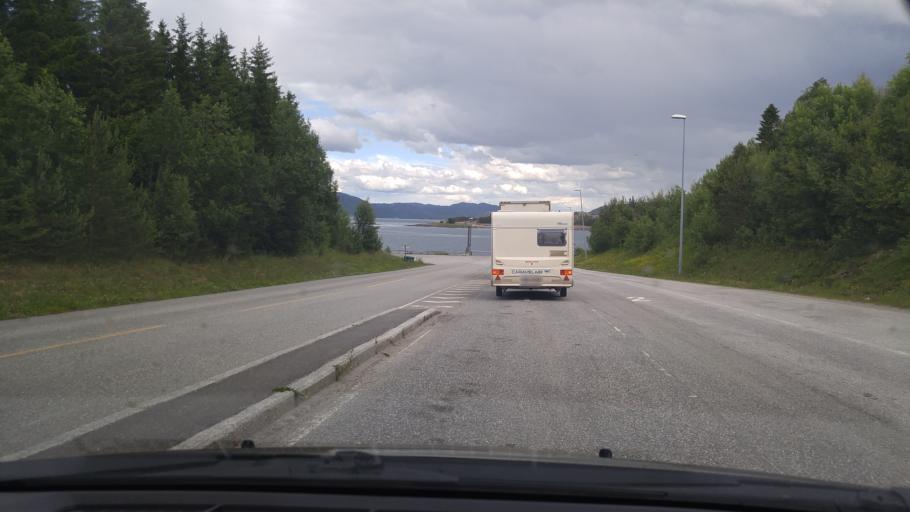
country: NO
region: Nord-Trondelag
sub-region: Naeroy
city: Kolvereid
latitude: 64.7676
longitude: 11.6210
